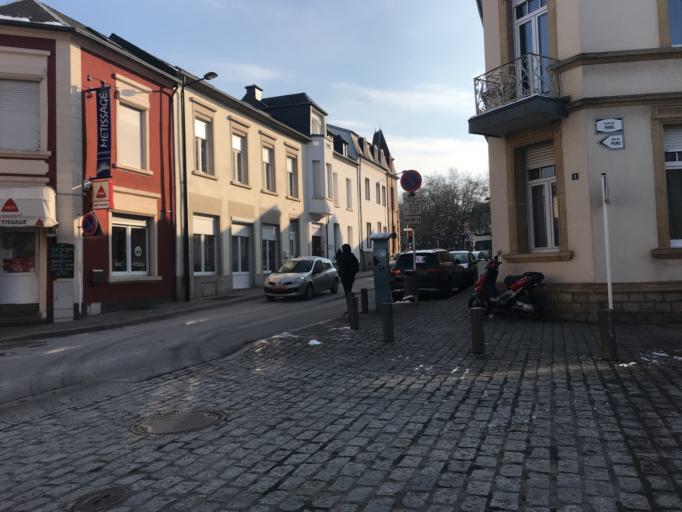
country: LU
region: Luxembourg
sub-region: Canton de Luxembourg
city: Luxembourg
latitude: 49.5981
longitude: 6.1400
